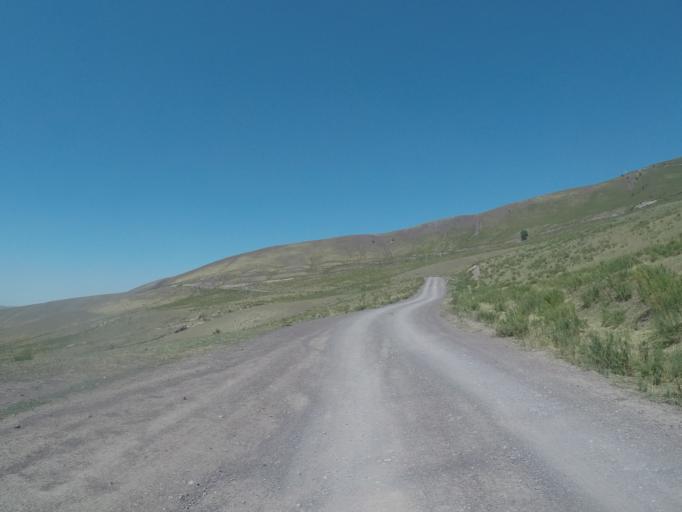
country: KG
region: Chuy
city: Bishkek
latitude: 42.6475
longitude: 74.5173
